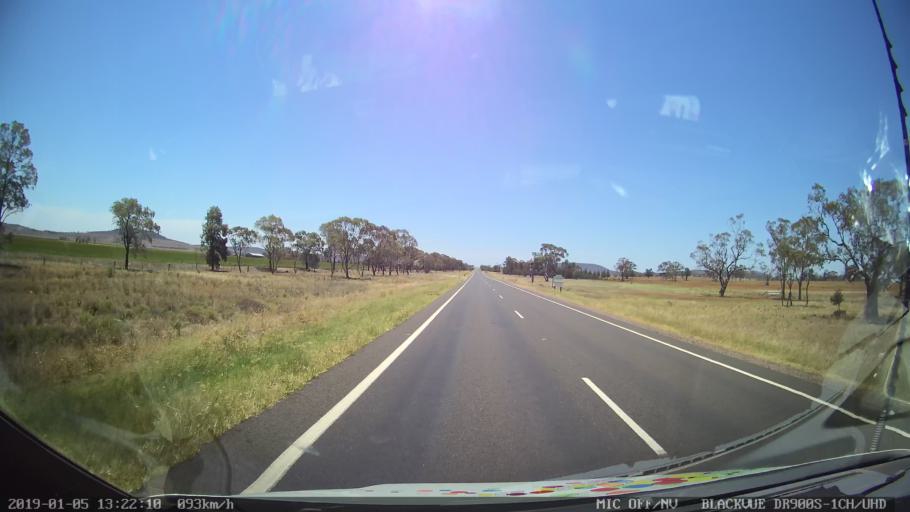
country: AU
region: New South Wales
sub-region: Gunnedah
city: Gunnedah
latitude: -31.0884
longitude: 149.9583
